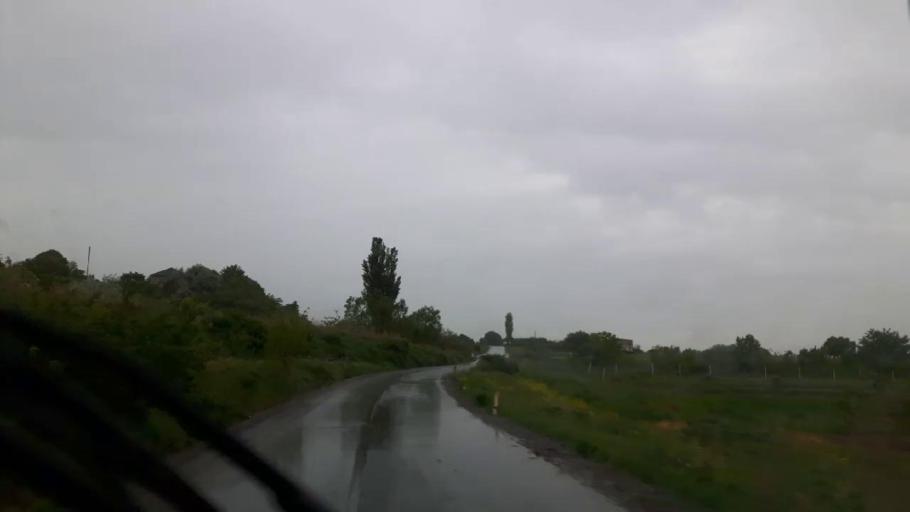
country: GE
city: Agara
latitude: 41.9832
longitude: 43.9624
